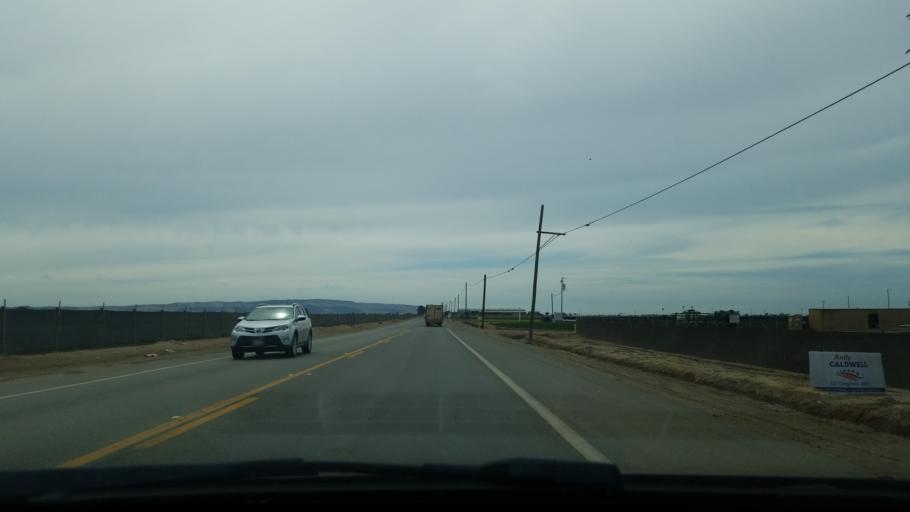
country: US
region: California
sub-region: Santa Barbara County
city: Santa Maria
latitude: 34.9237
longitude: -120.3856
